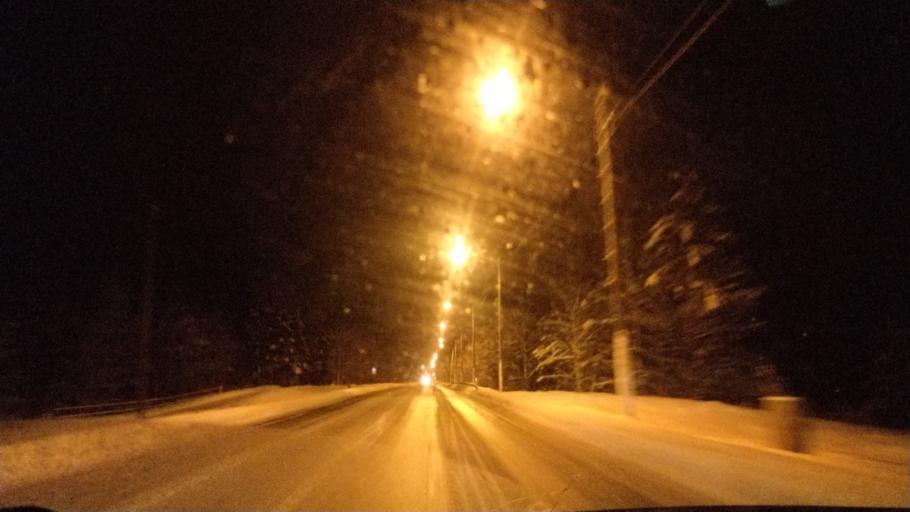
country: FI
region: Lapland
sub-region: Rovaniemi
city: Rovaniemi
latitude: 66.2666
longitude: 25.3339
